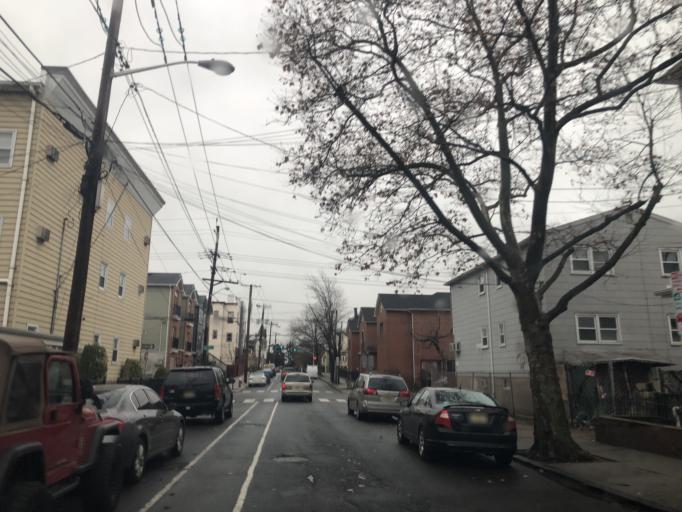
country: US
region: New Jersey
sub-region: Hudson County
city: Hoboken
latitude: 40.7480
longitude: -74.0436
